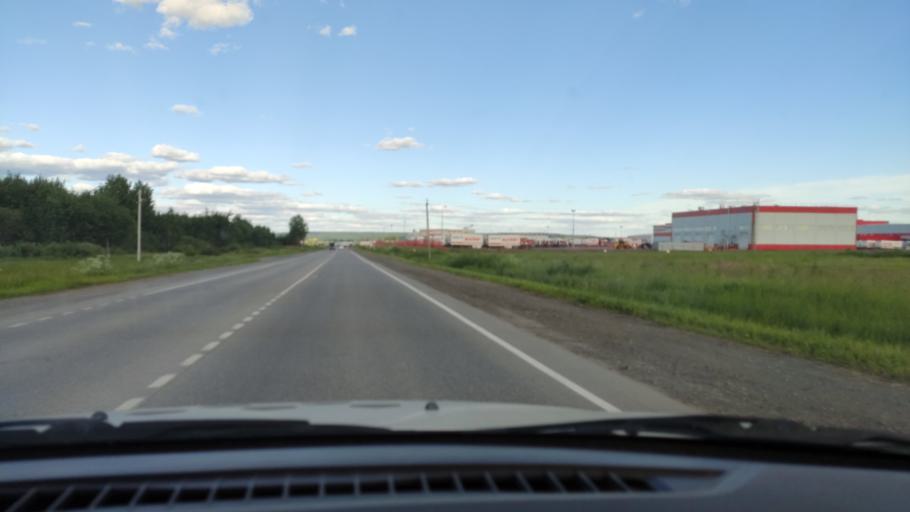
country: RU
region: Perm
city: Froly
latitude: 57.8979
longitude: 56.2395
